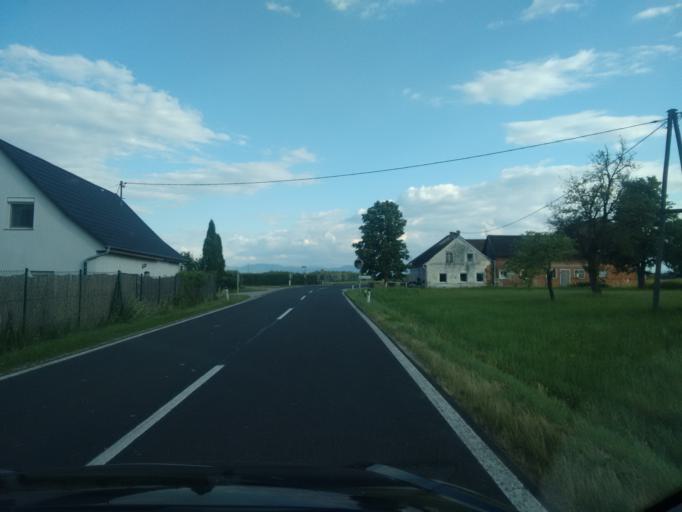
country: AT
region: Upper Austria
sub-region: Politischer Bezirk Steyr-Land
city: Sierning
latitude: 48.0778
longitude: 14.3202
